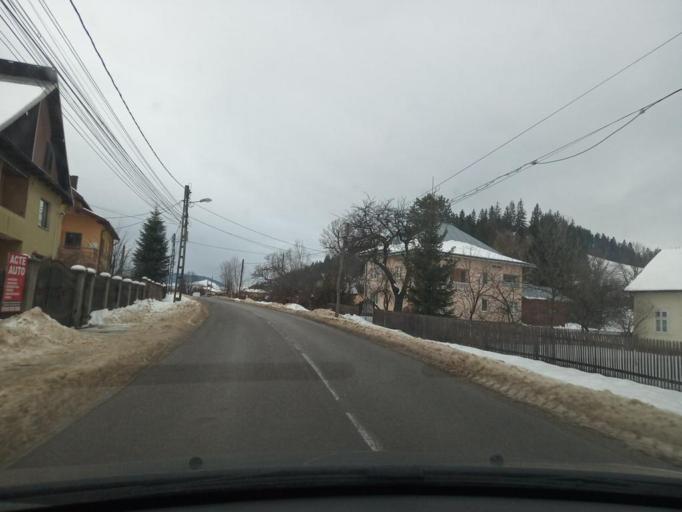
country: RO
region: Suceava
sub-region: Oras Gura Humorului
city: Gura Humorului
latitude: 47.5703
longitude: 25.8822
